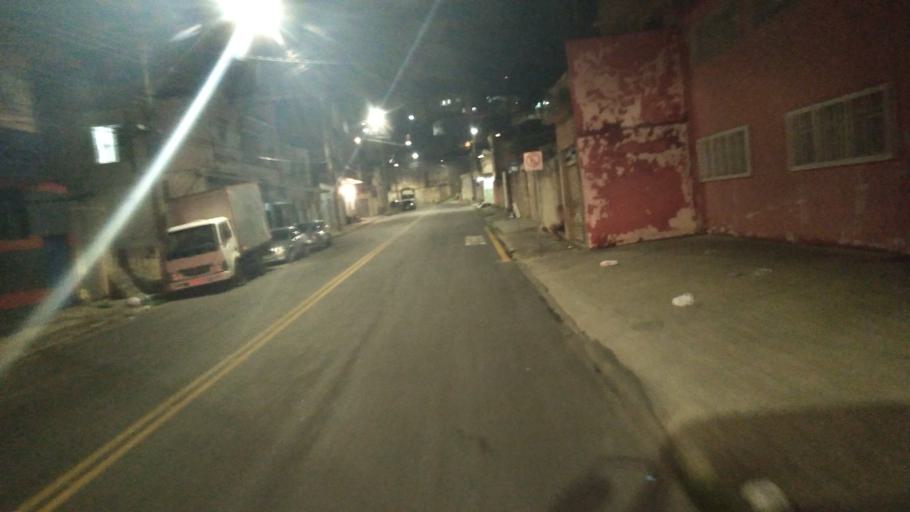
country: BR
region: Minas Gerais
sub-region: Belo Horizonte
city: Belo Horizonte
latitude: -19.9103
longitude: -43.9484
